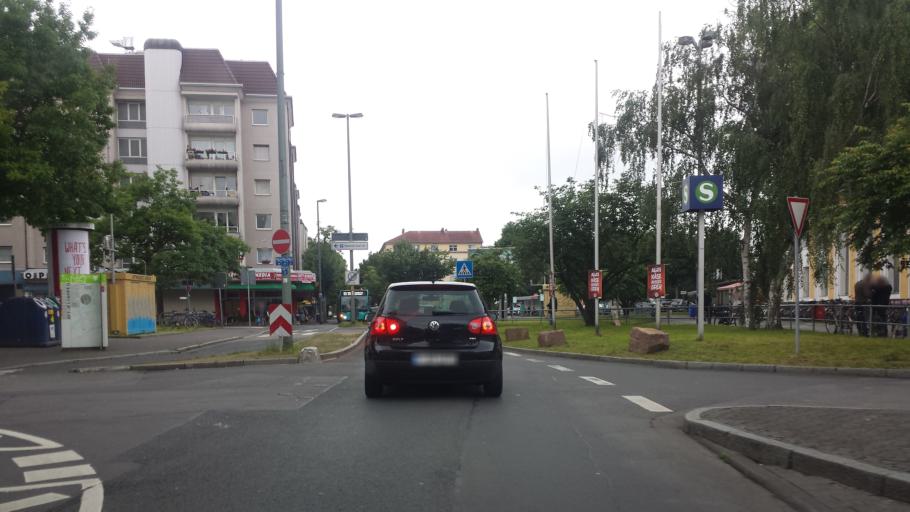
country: DE
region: Hesse
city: Sulzbach
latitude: 50.1020
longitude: 8.5430
